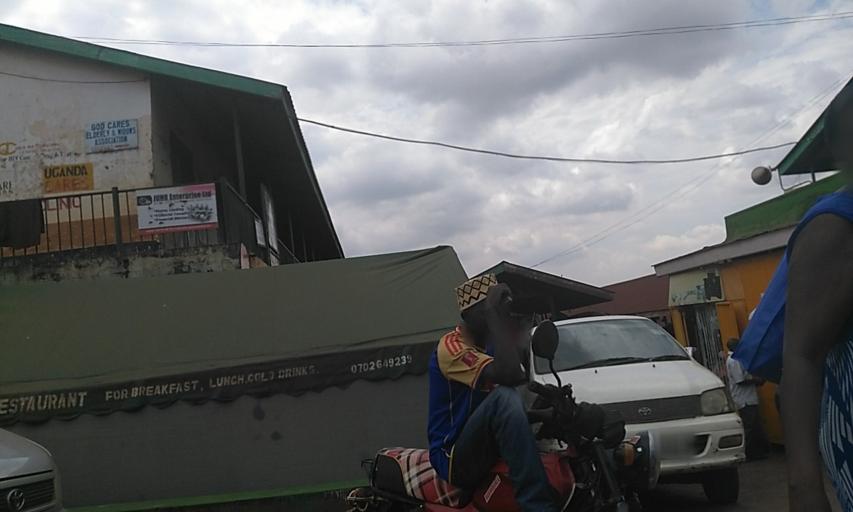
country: UG
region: Central Region
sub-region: Kampala District
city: Kampala
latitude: 0.3301
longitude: 32.6129
